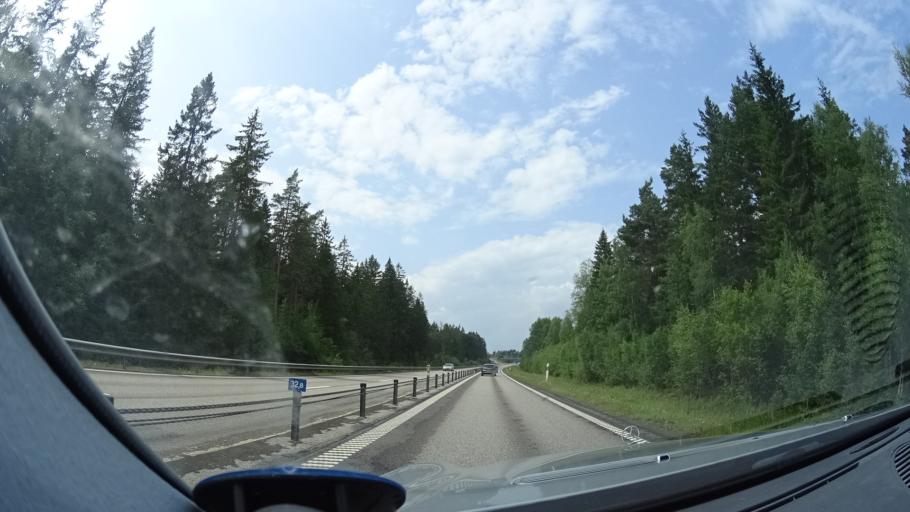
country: SE
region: Kalmar
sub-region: Nybro Kommun
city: Nybro
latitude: 56.7262
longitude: 15.8974
